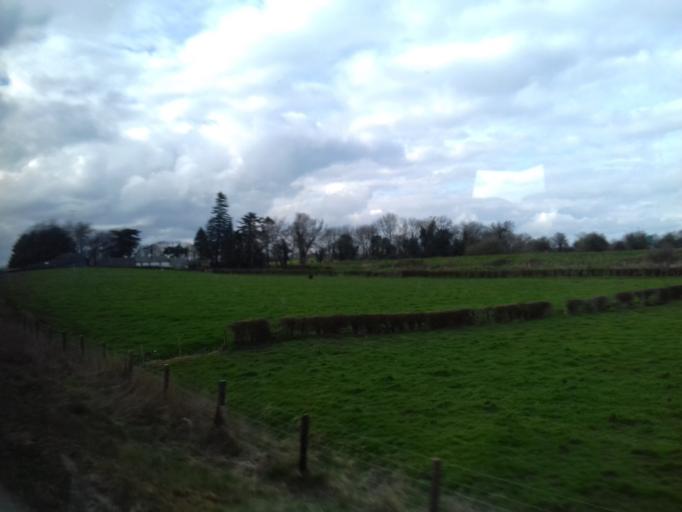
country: IE
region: Leinster
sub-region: An Iarmhi
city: Rathwire
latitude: 53.4919
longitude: -7.2165
